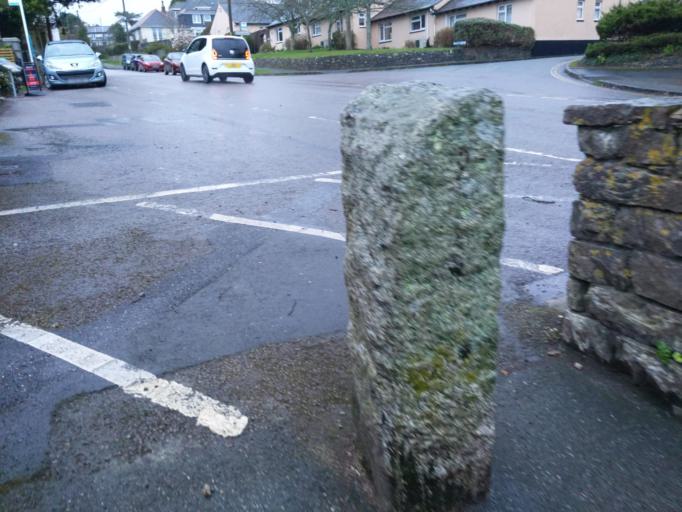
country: GB
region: England
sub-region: Devon
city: Wembury
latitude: 50.3167
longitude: -4.0363
